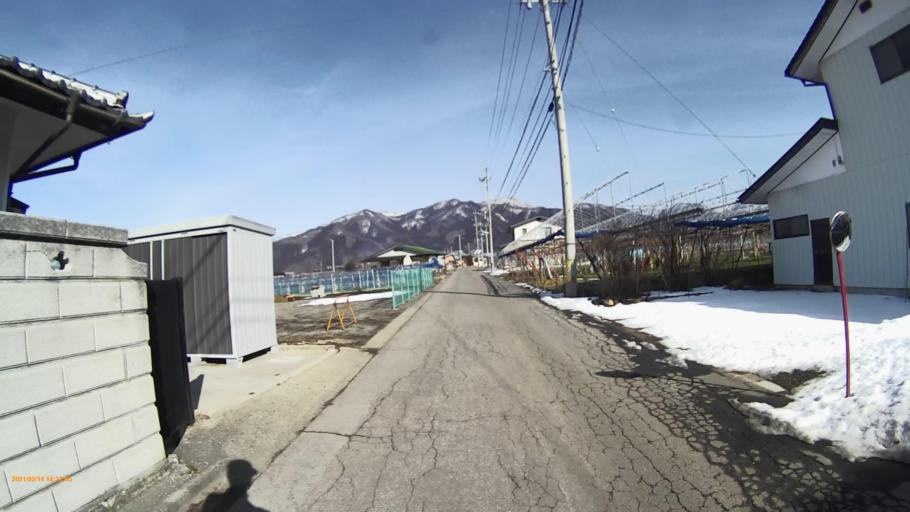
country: JP
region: Nagano
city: Nakano
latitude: 36.7433
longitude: 138.3978
